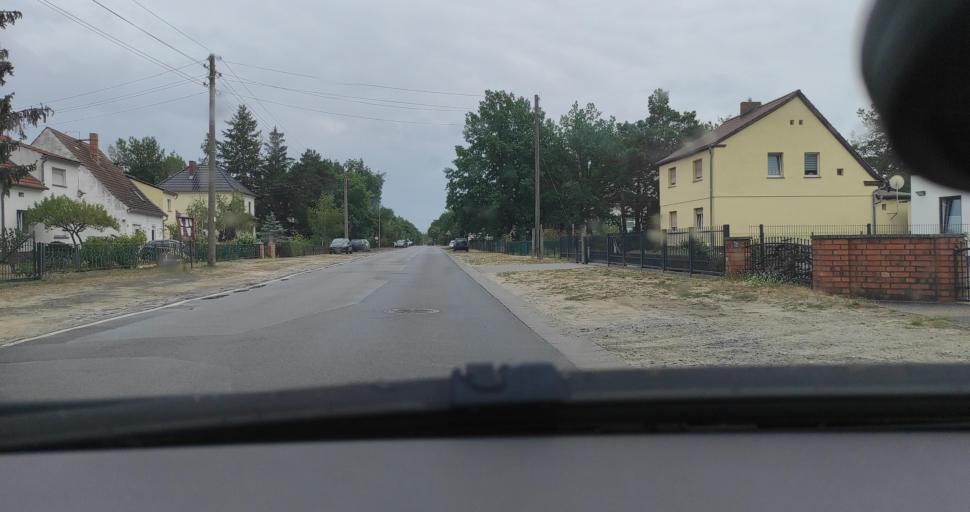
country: DE
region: Brandenburg
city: Cottbus
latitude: 51.7744
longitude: 14.3833
